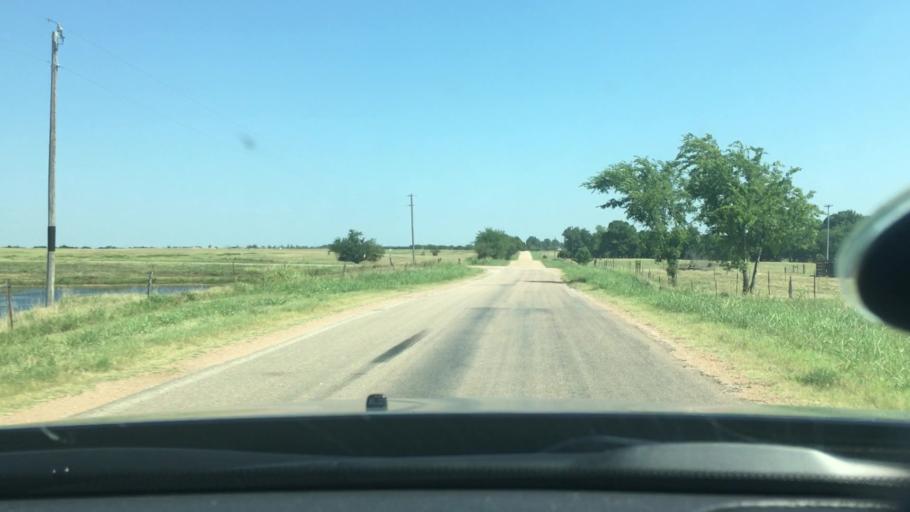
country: US
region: Oklahoma
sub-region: Johnston County
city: Tishomingo
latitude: 34.3166
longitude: -96.6359
